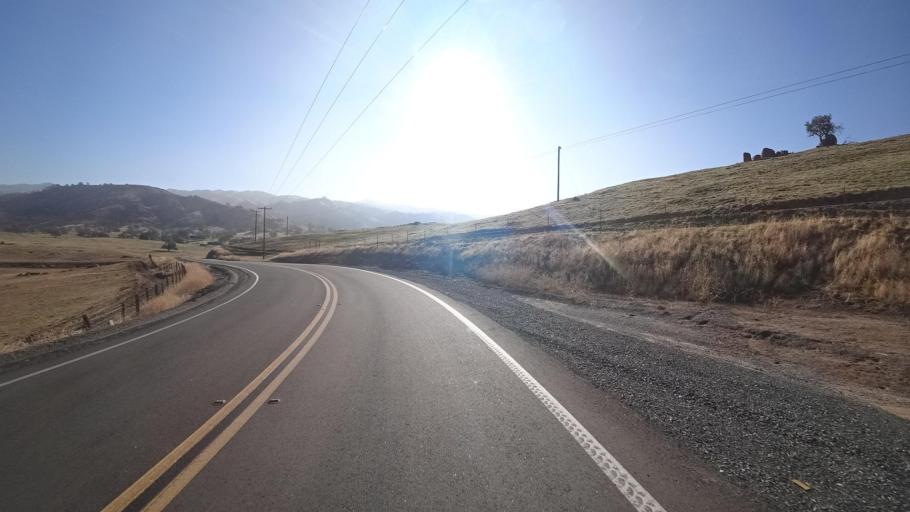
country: US
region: California
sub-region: Tulare County
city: Richgrove
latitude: 35.7113
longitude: -118.8446
